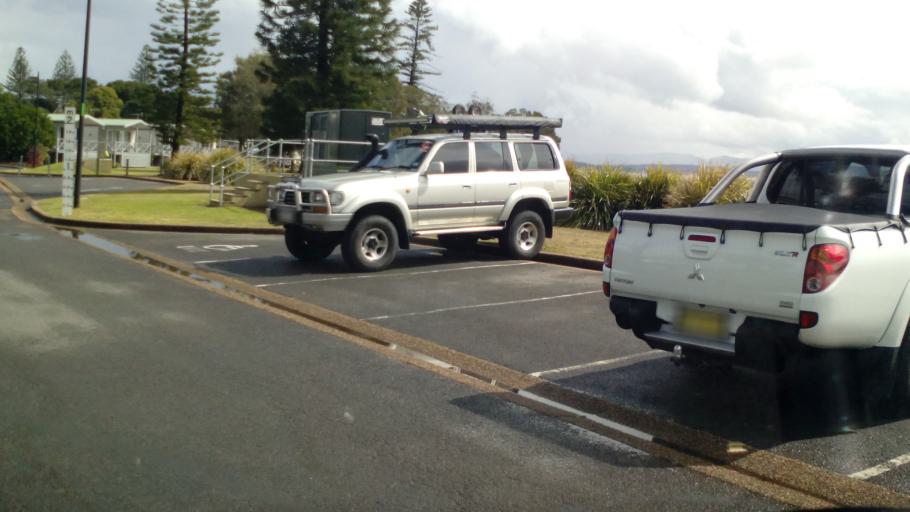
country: AU
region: New South Wales
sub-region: Lake Macquarie Shire
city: Belmont South
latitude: -33.0502
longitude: 151.6524
